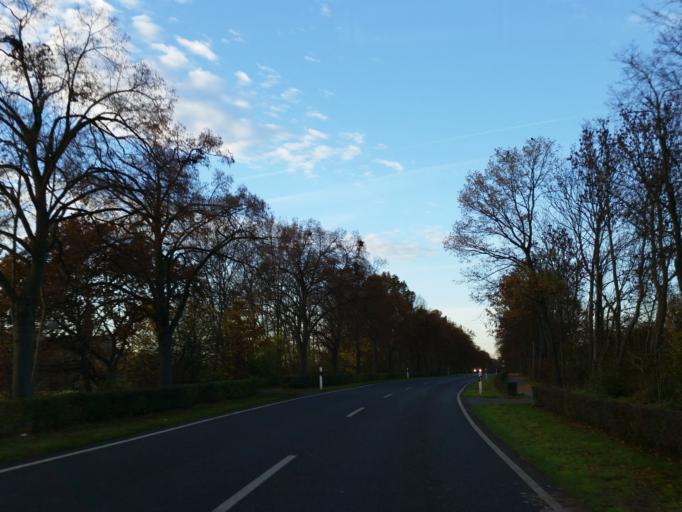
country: DE
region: Lower Saxony
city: Braunschweig
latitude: 52.2655
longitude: 10.5826
